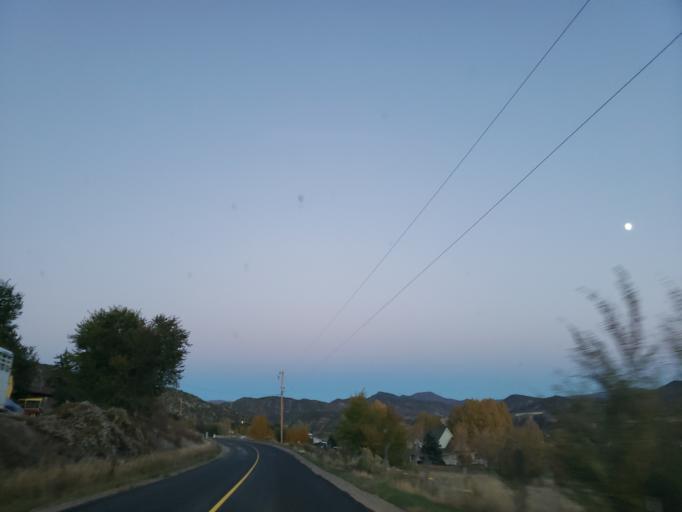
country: US
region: Colorado
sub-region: Garfield County
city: New Castle
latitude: 39.5586
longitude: -107.5798
